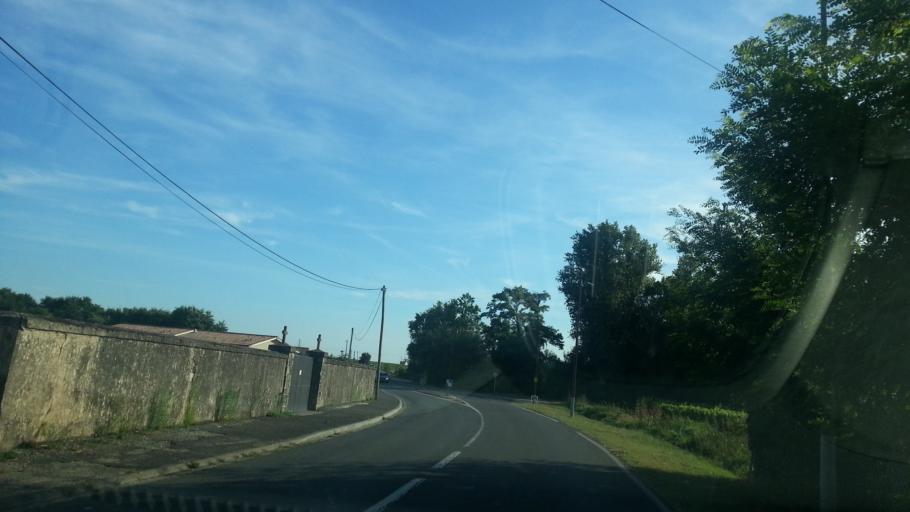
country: FR
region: Aquitaine
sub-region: Departement de la Gironde
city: Podensac
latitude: 44.6451
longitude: -0.3583
